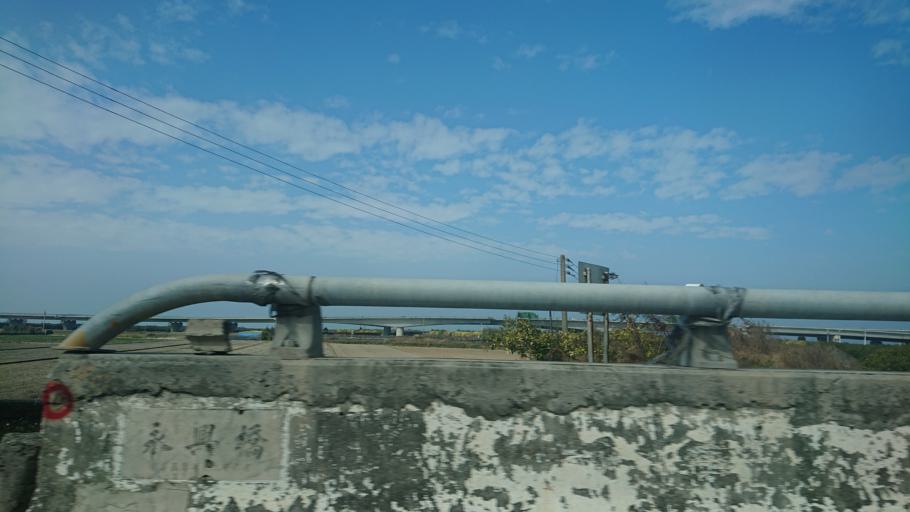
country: TW
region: Taiwan
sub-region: Changhua
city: Chang-hua
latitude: 23.9335
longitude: 120.3226
